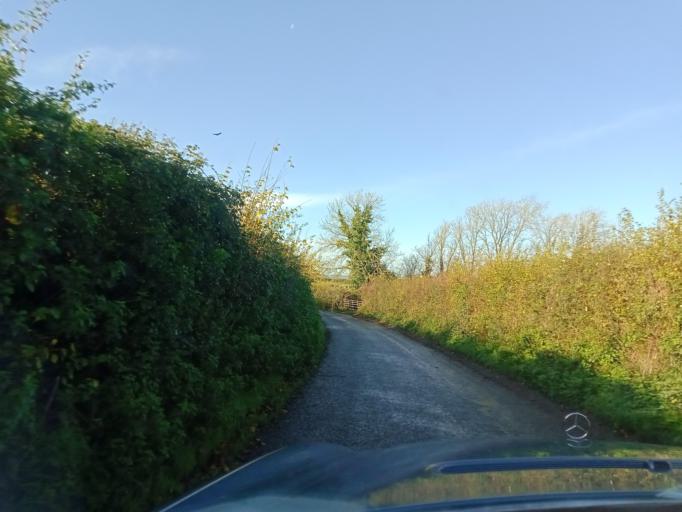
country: IE
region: Leinster
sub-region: Kilkenny
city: Mooncoin
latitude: 52.3001
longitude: -7.2111
